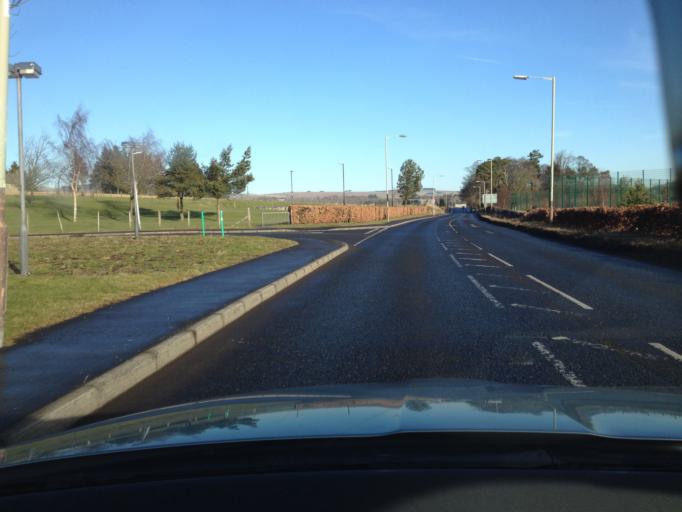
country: GB
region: Scotland
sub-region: Perth and Kinross
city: Milnathort
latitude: 56.2179
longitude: -3.4263
